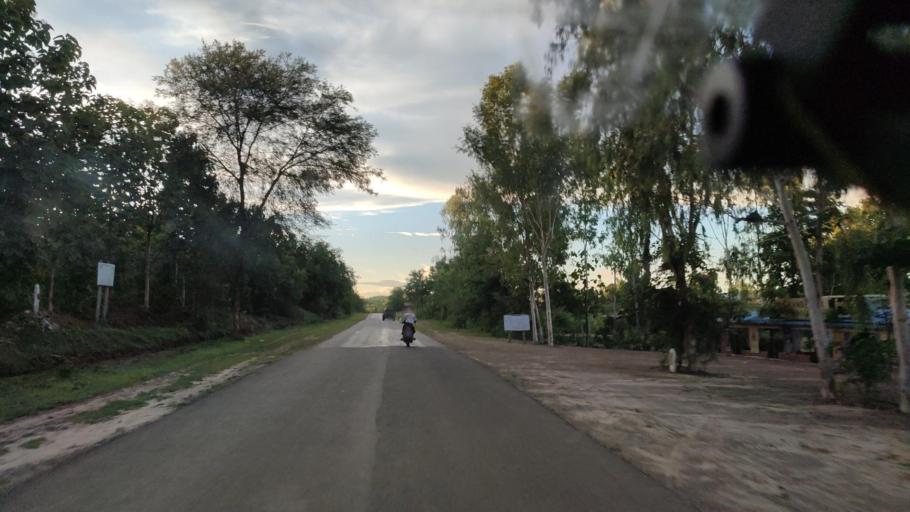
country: MM
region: Magway
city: Taungdwingyi
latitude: 20.1325
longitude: 95.6674
